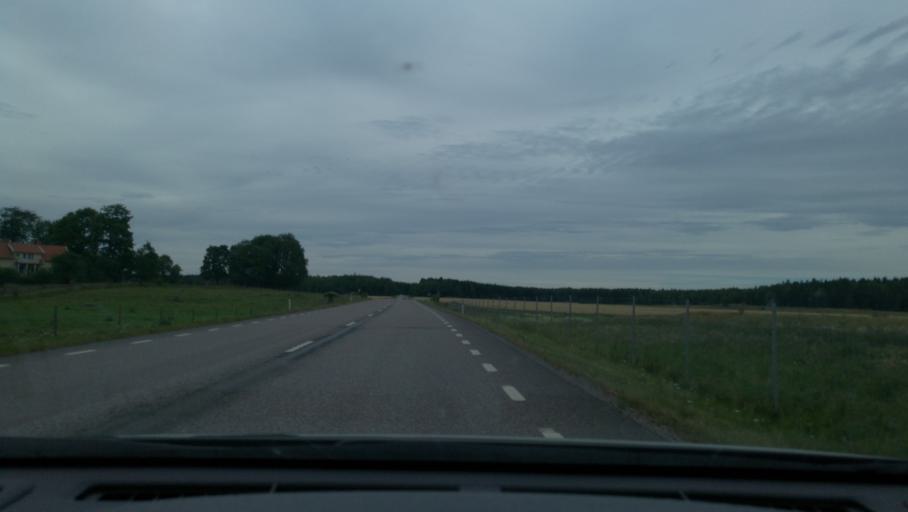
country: SE
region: Soedermanland
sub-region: Katrineholms Kommun
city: Katrineholm
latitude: 59.0175
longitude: 16.2146
